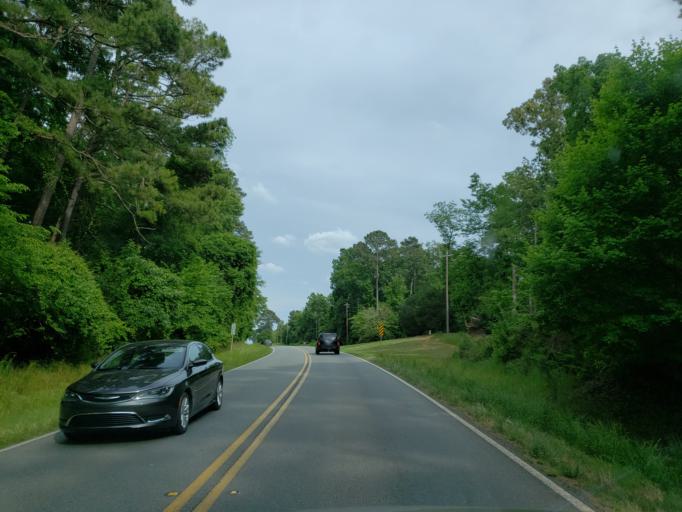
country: US
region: Georgia
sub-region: Dooly County
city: Vienna
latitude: 32.1136
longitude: -83.8587
